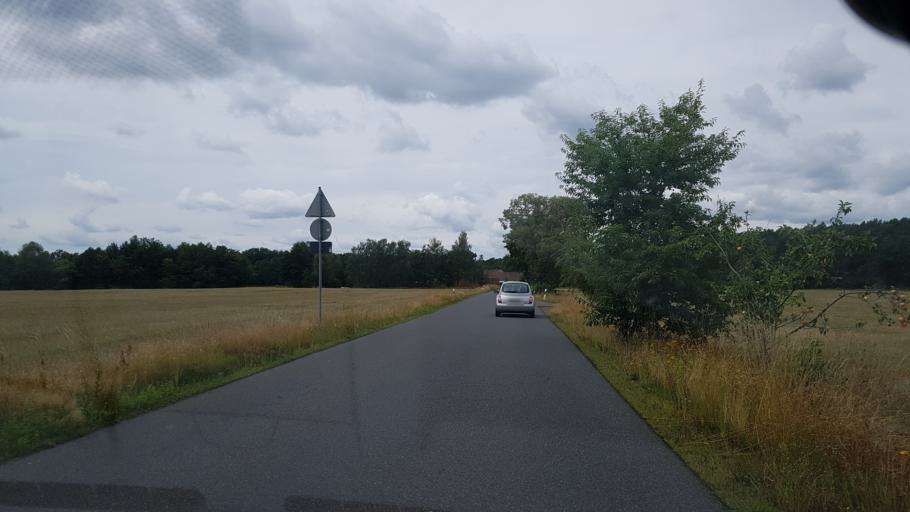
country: DE
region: Brandenburg
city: Spremberg
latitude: 51.5038
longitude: 14.4122
